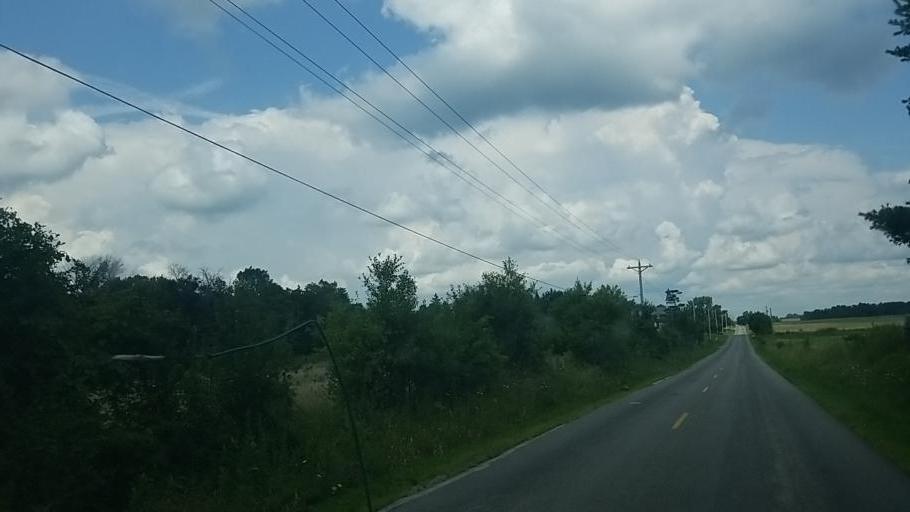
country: US
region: Ohio
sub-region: Medina County
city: Lodi
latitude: 41.0469
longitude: -82.0770
